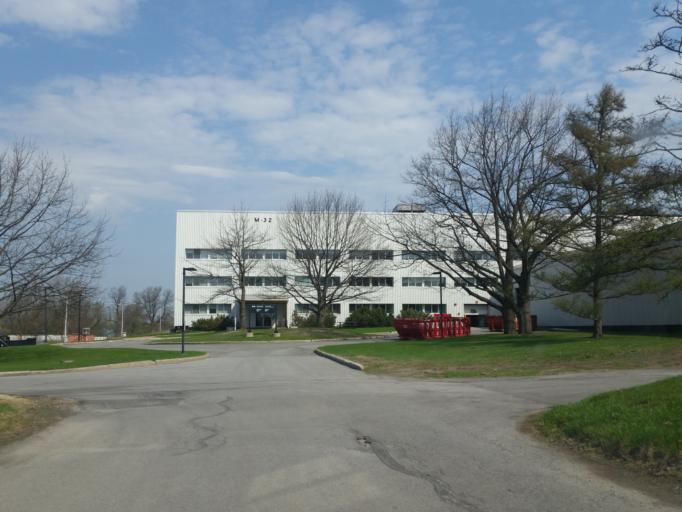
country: CA
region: Quebec
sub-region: Outaouais
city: Gatineau
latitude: 45.4509
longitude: -75.6218
